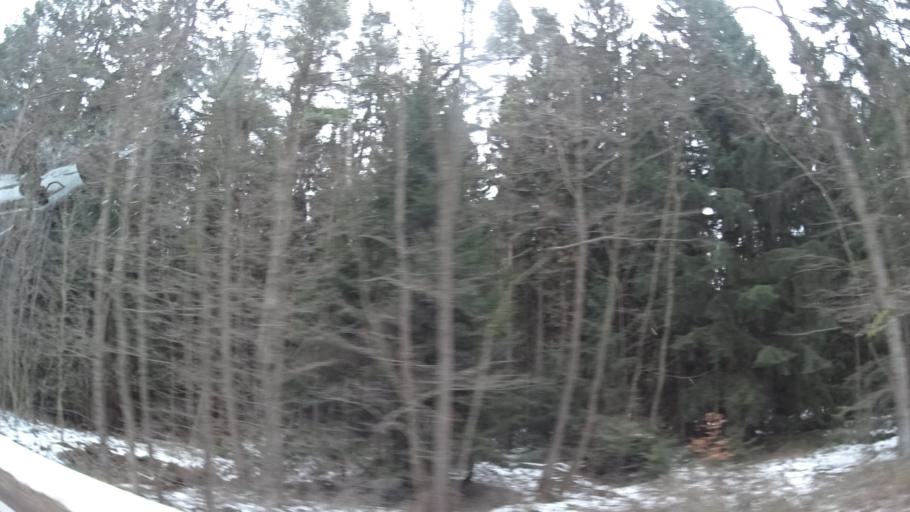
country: DE
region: Thuringia
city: Pennewitz
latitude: 50.6732
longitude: 11.0387
